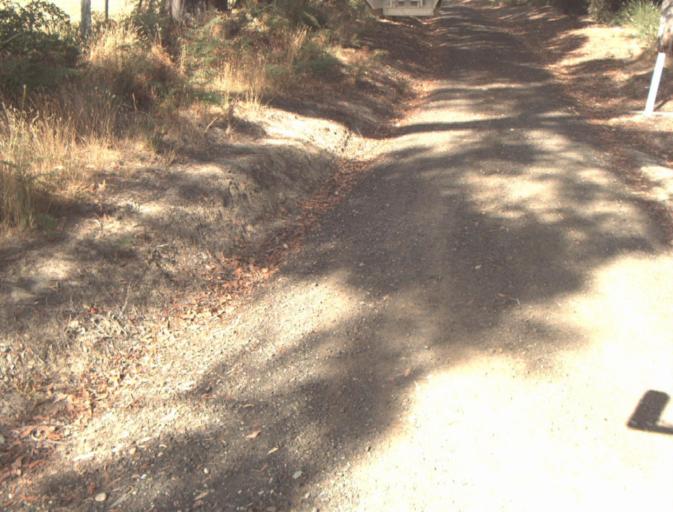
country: AU
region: Tasmania
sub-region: Dorset
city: Bridport
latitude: -41.1520
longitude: 147.2293
